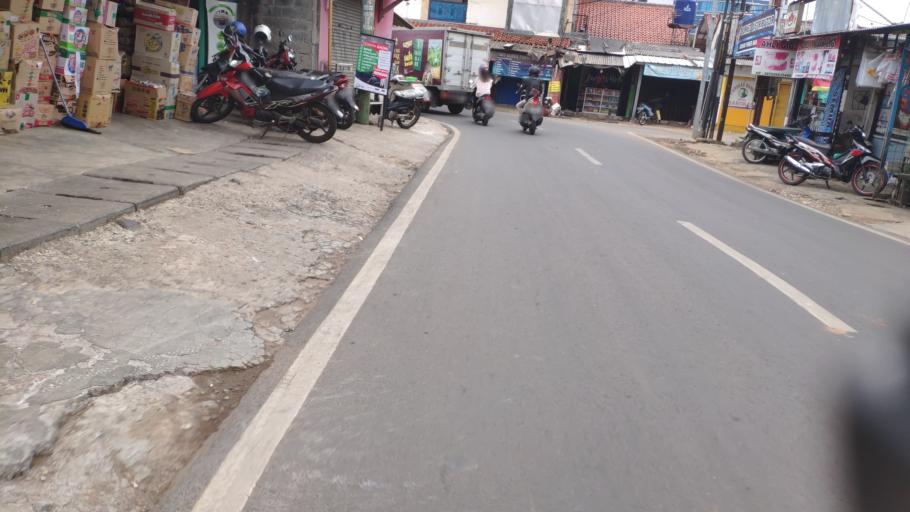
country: ID
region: West Java
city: Depok
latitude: -6.3464
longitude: 106.8255
